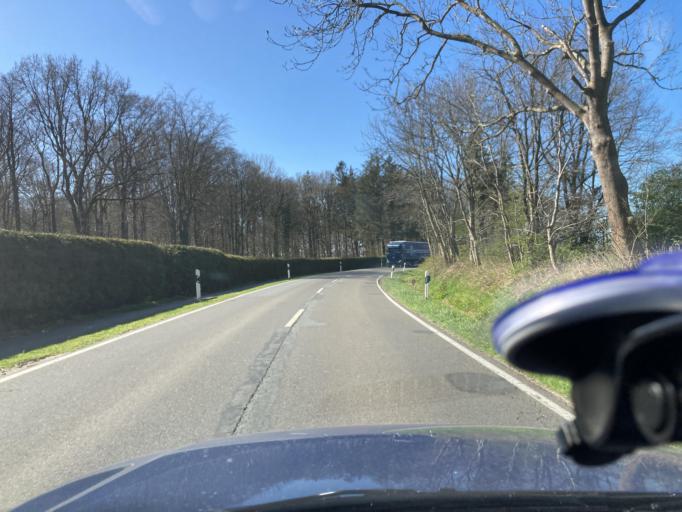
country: DE
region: Schleswig-Holstein
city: Odderade
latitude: 54.1364
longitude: 9.1889
